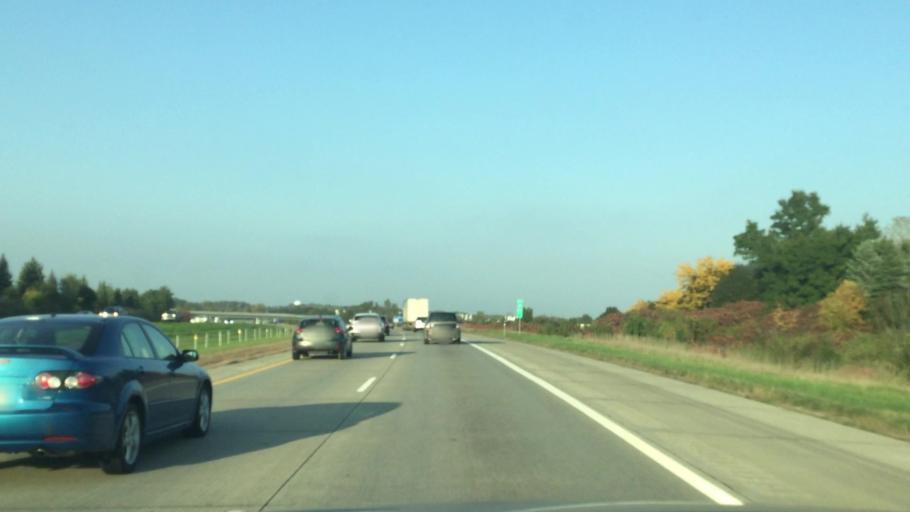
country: US
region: Michigan
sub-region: Wayne County
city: Plymouth
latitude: 42.3713
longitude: -83.5389
